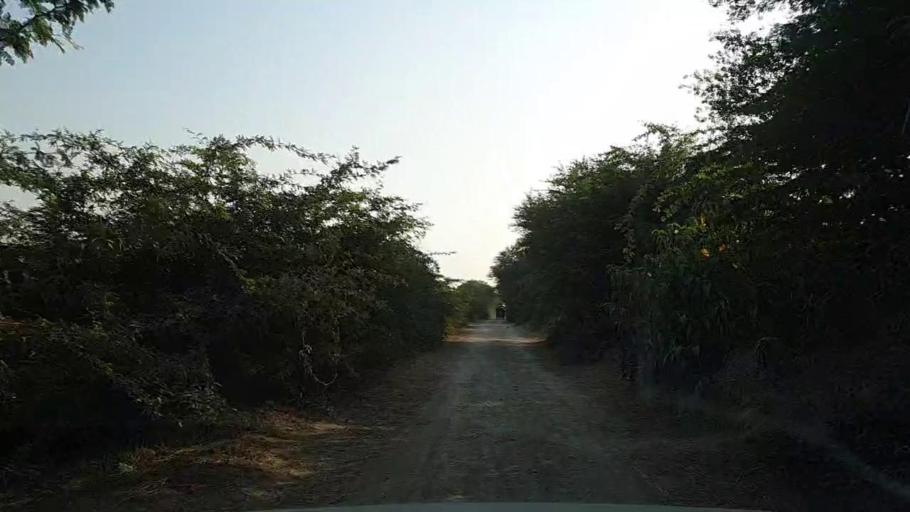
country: PK
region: Sindh
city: Mirpur Batoro
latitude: 24.7681
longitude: 68.2342
